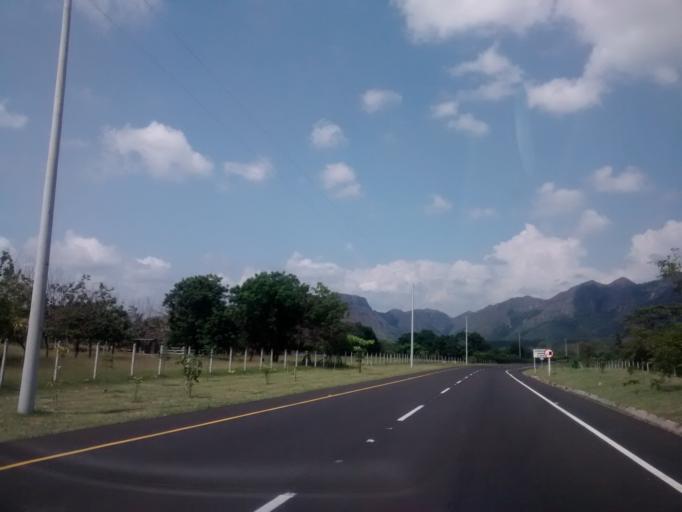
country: CO
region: Tolima
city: Valle de San Juan
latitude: 4.2635
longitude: -74.9970
